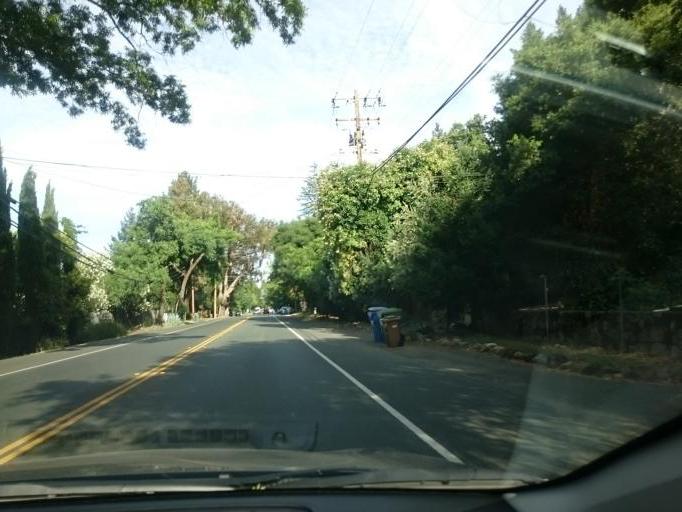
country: US
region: California
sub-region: Napa County
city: Calistoga
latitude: 38.5772
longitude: -122.5861
